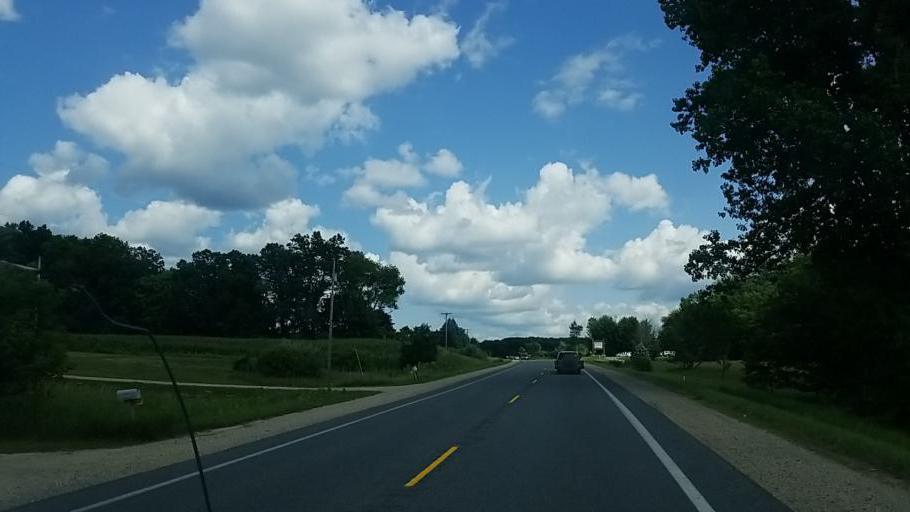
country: US
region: Michigan
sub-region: Newaygo County
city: Newaygo
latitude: 43.3962
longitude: -85.6490
